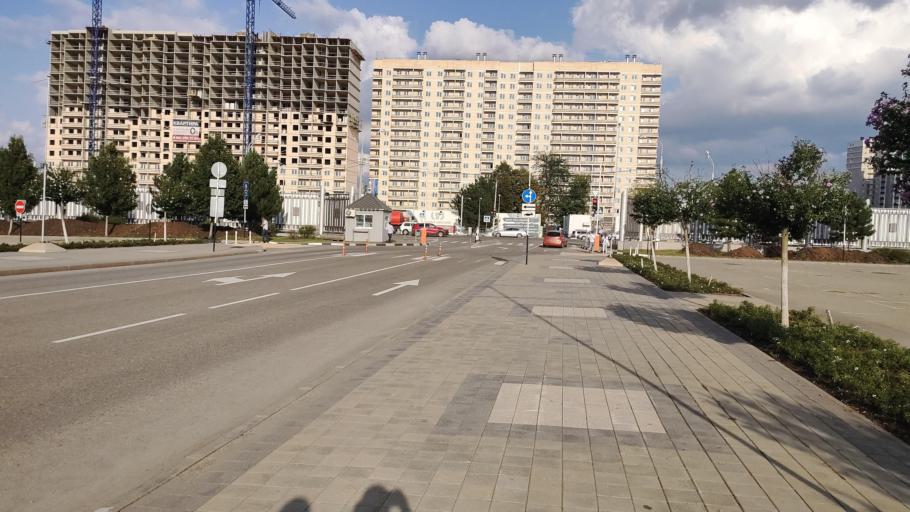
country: RU
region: Krasnodarskiy
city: Krasnodar
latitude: 45.1169
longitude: 38.9844
